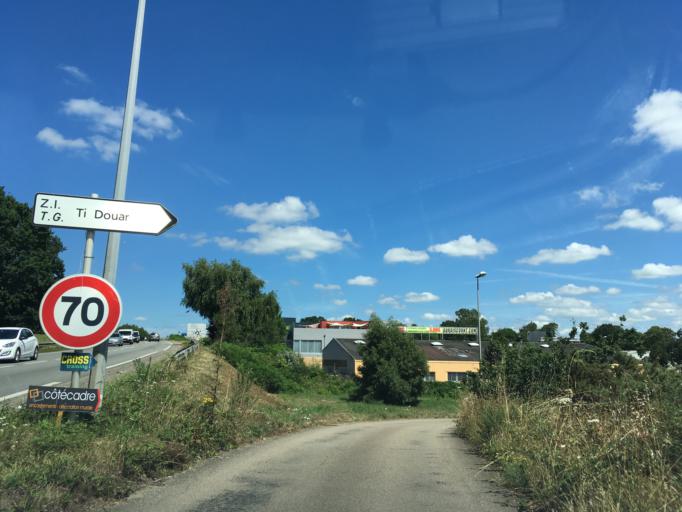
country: FR
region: Brittany
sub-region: Departement du Finistere
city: Quimper
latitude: 47.9810
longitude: -4.0780
